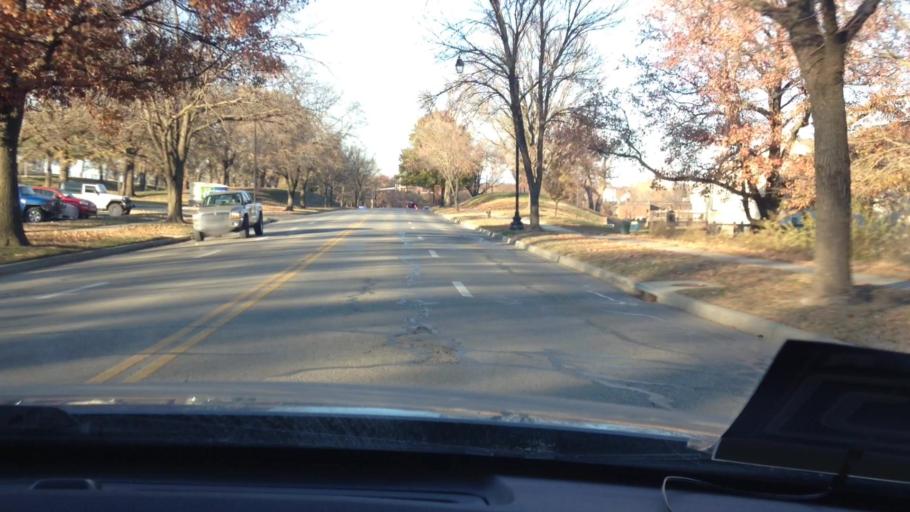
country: US
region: Kansas
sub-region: Leavenworth County
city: Leavenworth
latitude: 39.3417
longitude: -94.9211
